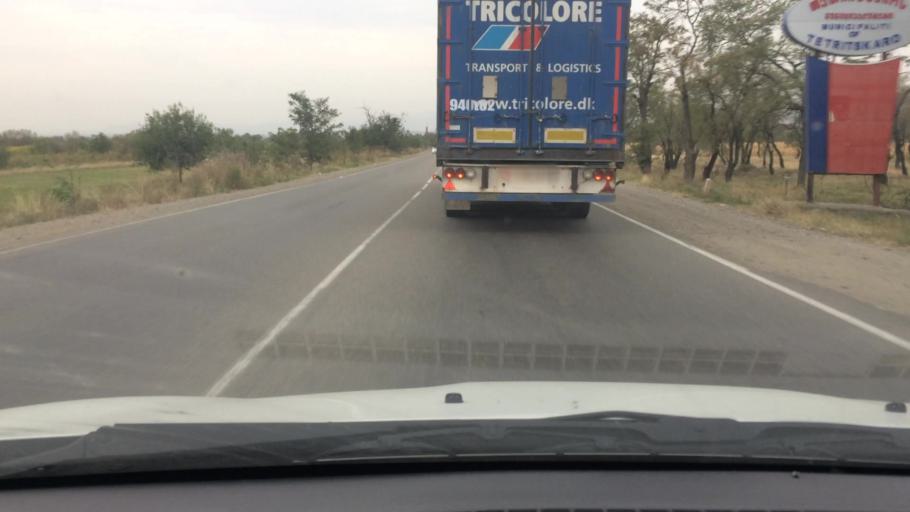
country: GE
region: T'bilisi
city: Tbilisi
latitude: 41.5908
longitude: 44.7802
